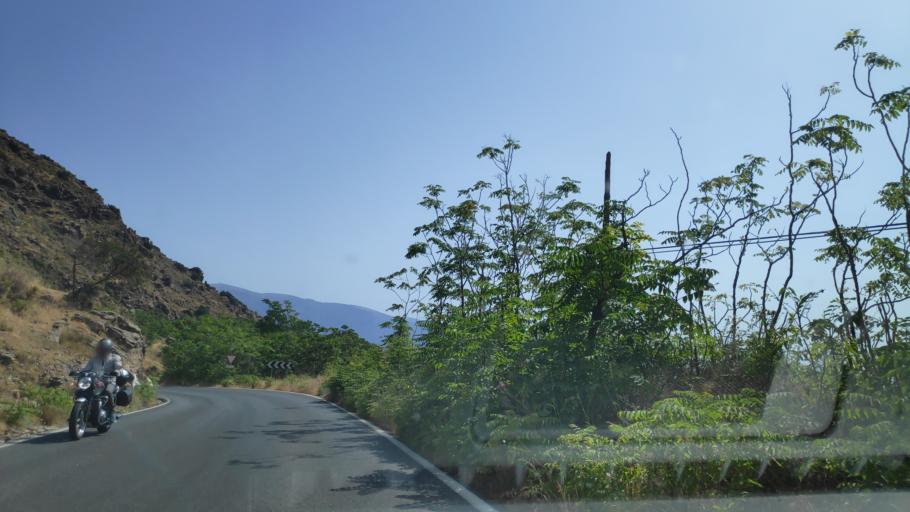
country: ES
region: Andalusia
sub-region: Provincia de Granada
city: Pampaneira
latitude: 36.9316
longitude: -3.3640
